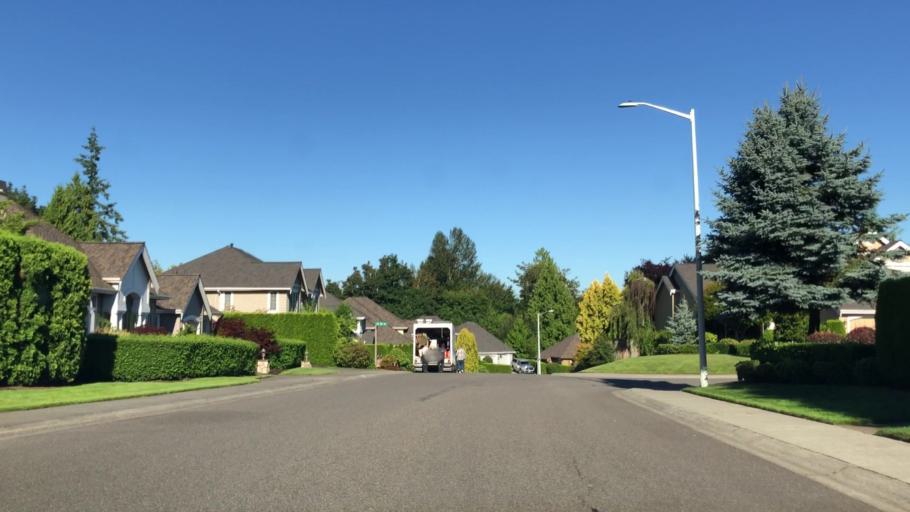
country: US
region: Washington
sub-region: Snohomish County
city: North Creek
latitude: 47.8141
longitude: -122.1974
